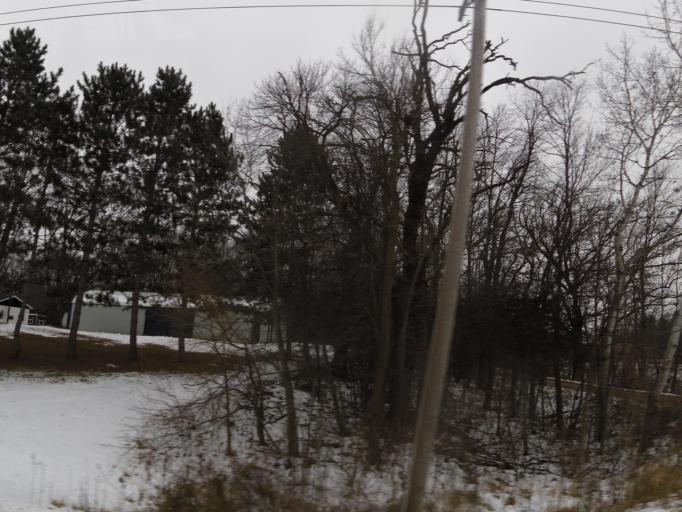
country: US
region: Minnesota
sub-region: Carver County
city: Carver
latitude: 44.7178
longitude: -93.6705
